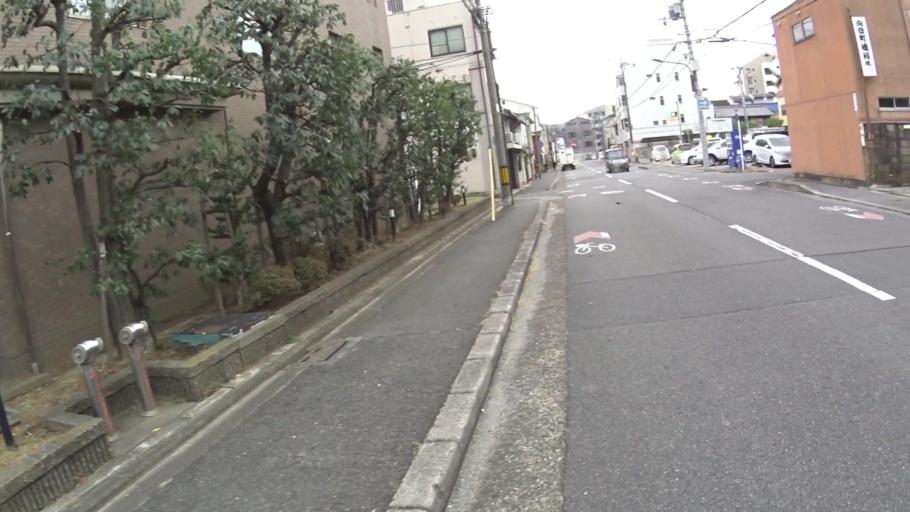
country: JP
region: Kyoto
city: Kyoto
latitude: 34.9905
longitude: 135.7459
